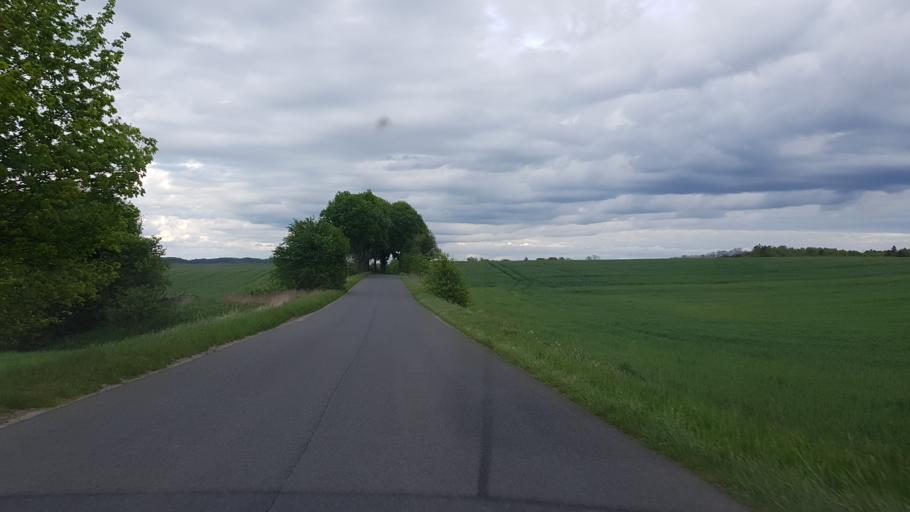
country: PL
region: West Pomeranian Voivodeship
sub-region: Powiat slawienski
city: Slawno
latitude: 54.2735
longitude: 16.5384
